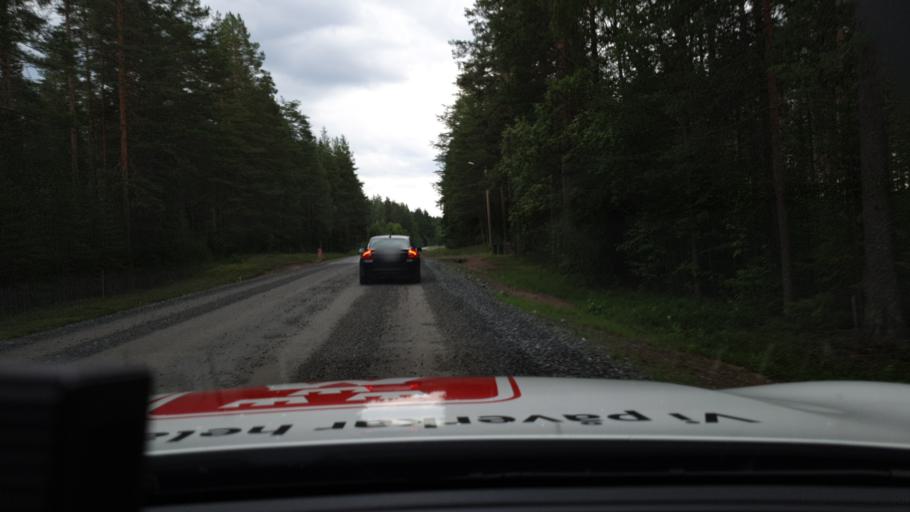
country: SE
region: Norrbotten
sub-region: Bodens Kommun
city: Boden
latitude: 65.8790
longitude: 21.4048
